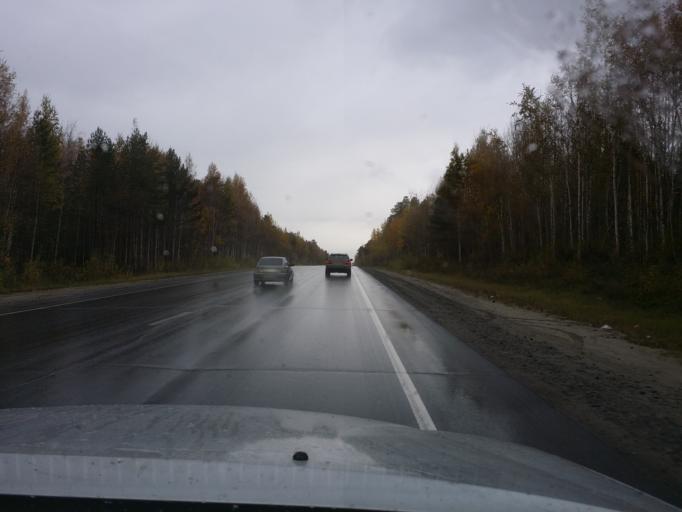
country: RU
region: Khanty-Mansiyskiy Avtonomnyy Okrug
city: Megion
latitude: 61.0550
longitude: 76.3069
